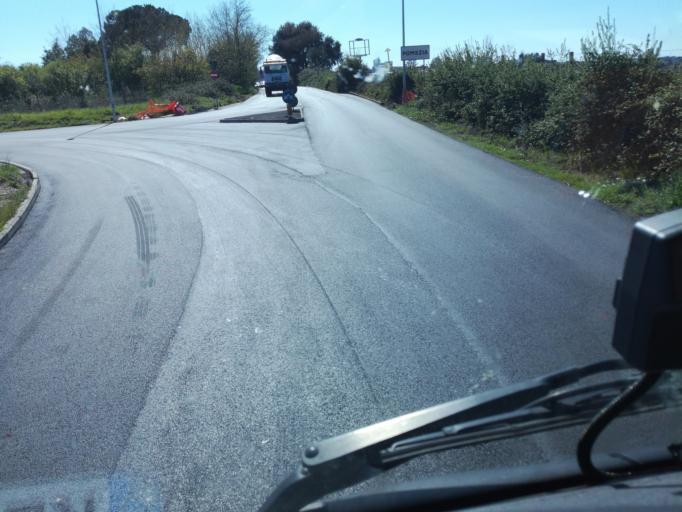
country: IT
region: Latium
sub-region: Citta metropolitana di Roma Capitale
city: Area Produttiva
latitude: 41.6953
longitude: 12.5233
